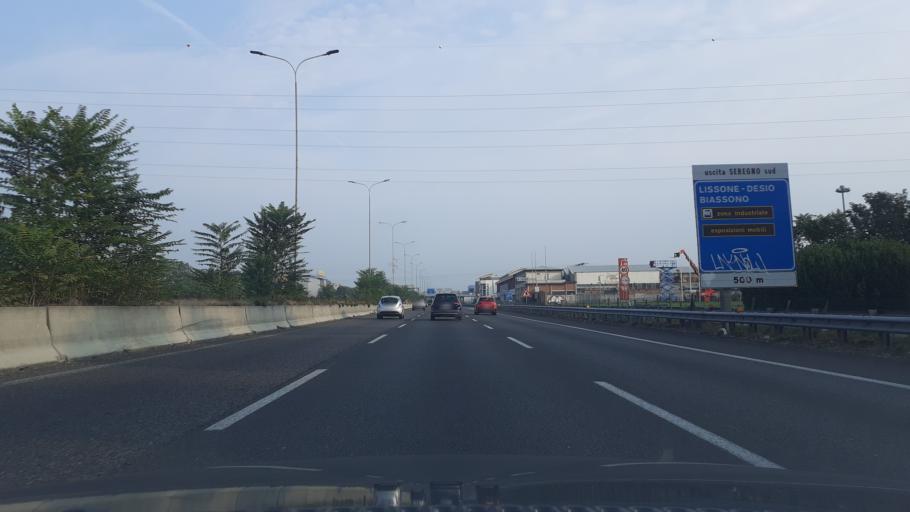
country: IT
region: Lombardy
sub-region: Provincia di Monza e Brianza
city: Santa Margherita
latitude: 45.6299
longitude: 9.2249
